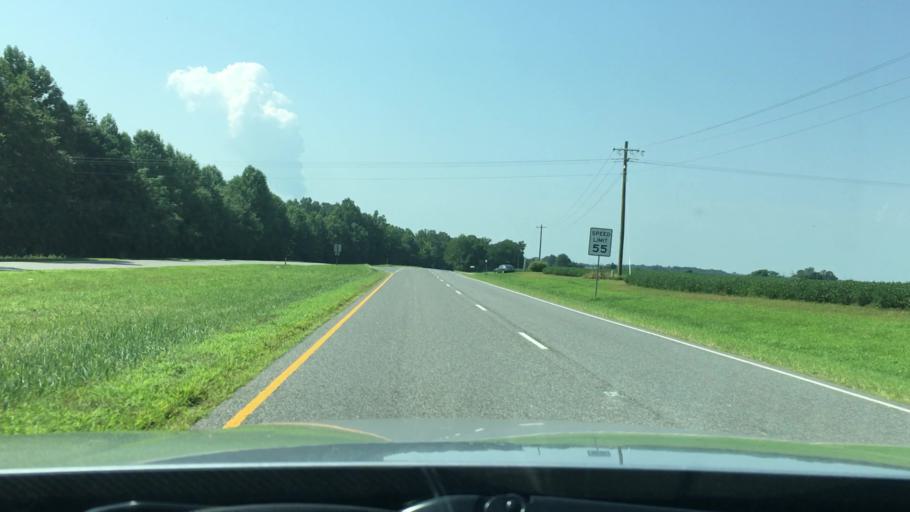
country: US
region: Virginia
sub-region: Caroline County
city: Bowling Green
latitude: 37.9868
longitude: -77.4187
